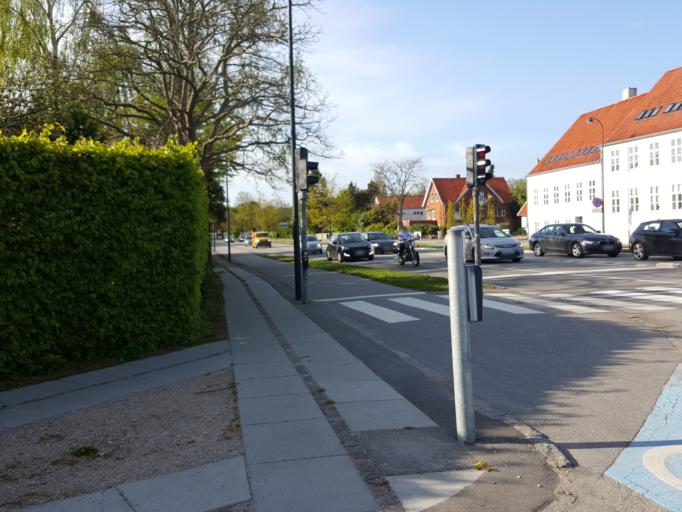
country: DK
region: Capital Region
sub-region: Rudersdal Kommune
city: Holte
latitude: 55.8201
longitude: 12.4663
